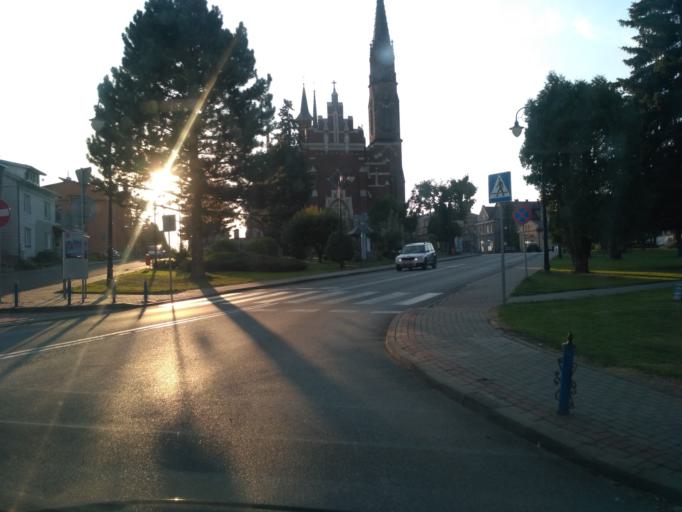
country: PL
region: Subcarpathian Voivodeship
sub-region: Powiat krosnienski
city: Korczyna
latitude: 49.7144
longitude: 21.8112
